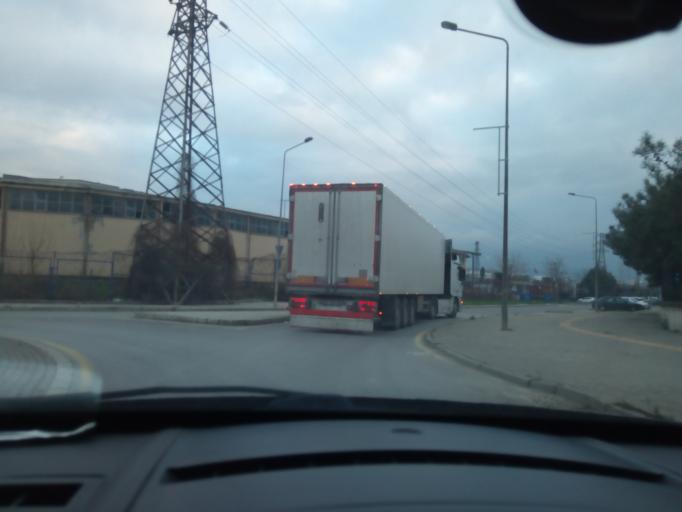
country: TR
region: Bursa
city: Niluefer
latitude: 40.2379
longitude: 28.9684
